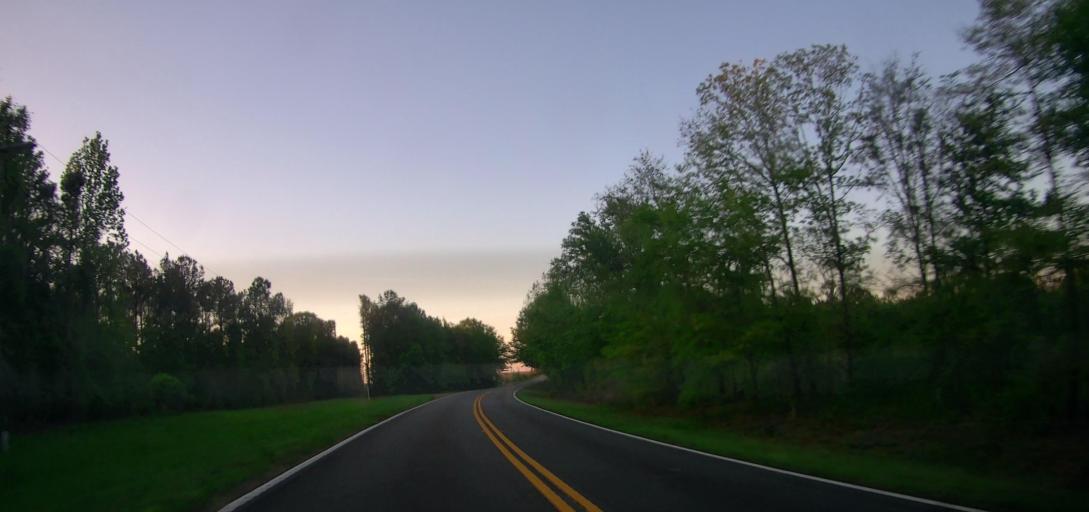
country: US
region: Georgia
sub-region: Marion County
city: Buena Vista
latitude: 32.3768
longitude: -84.5581
